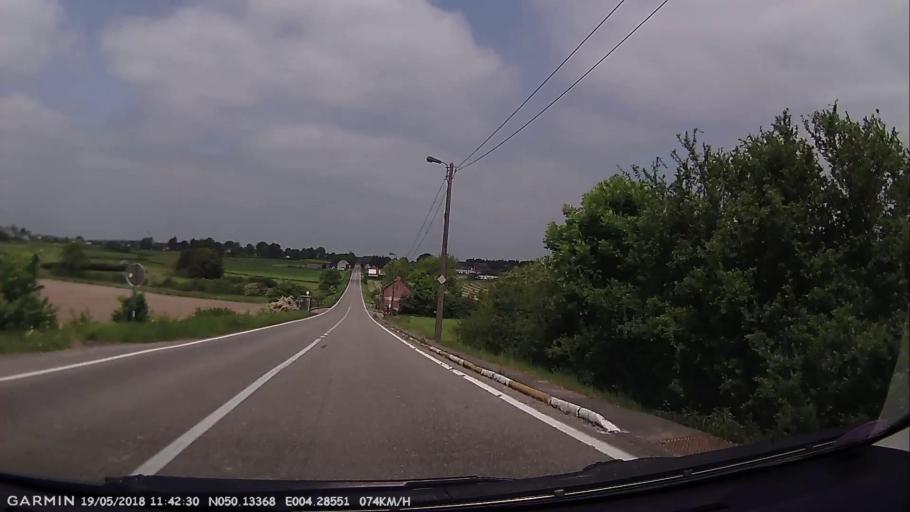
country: BE
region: Wallonia
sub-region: Province du Hainaut
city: Froidchapelle
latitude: 50.1338
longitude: 4.2854
